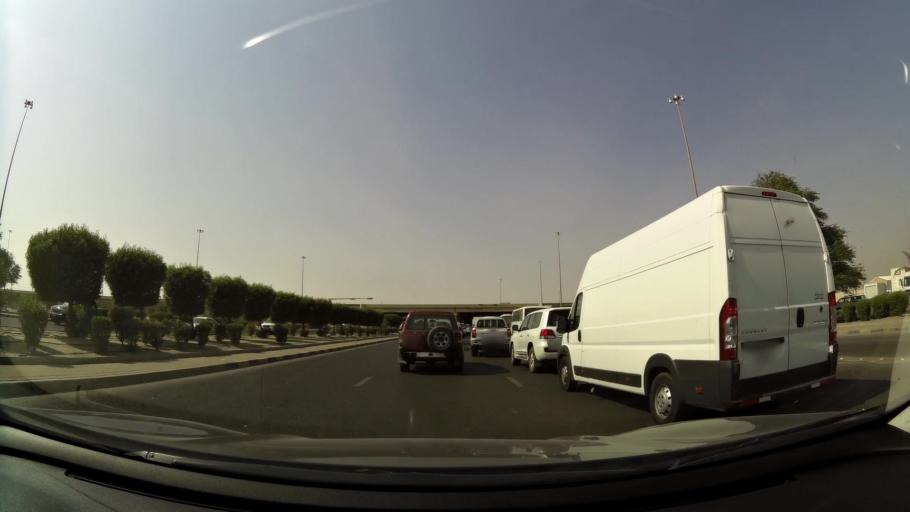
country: KW
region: Al Ahmadi
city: Al Fahahil
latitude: 29.0717
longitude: 48.1130
